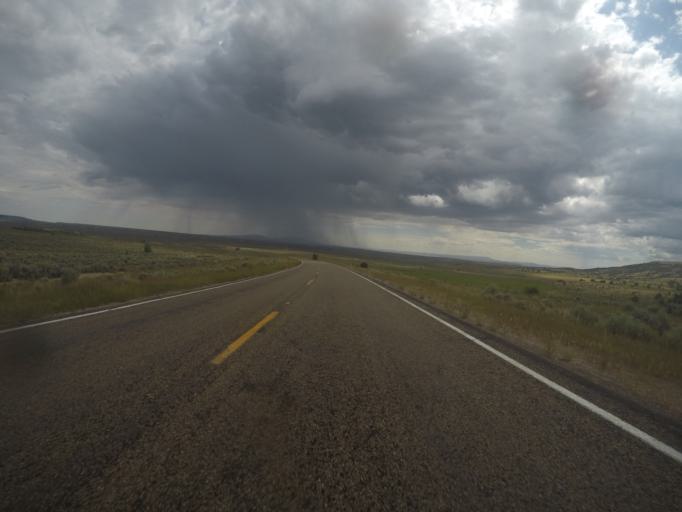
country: US
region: Utah
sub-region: Daggett County
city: Manila
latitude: 41.0229
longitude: -109.8937
